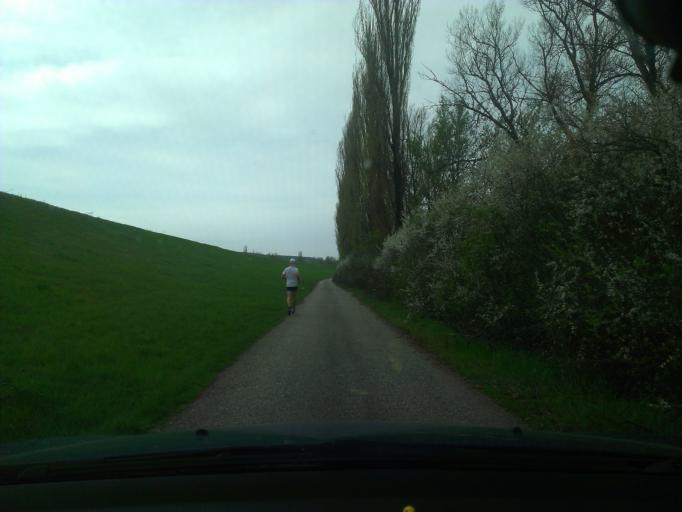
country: SK
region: Trnavsky
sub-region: Okres Trnava
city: Piestany
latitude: 48.5239
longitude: 17.8156
